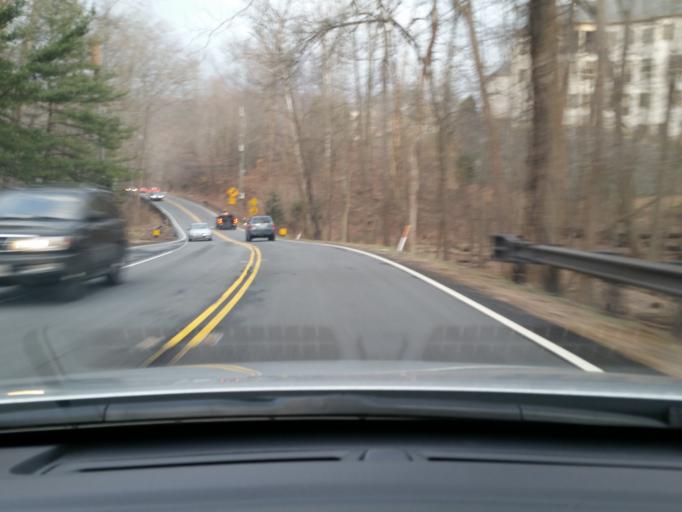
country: US
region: Virginia
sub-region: Fairfax County
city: McLean
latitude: 38.9591
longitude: -77.2085
